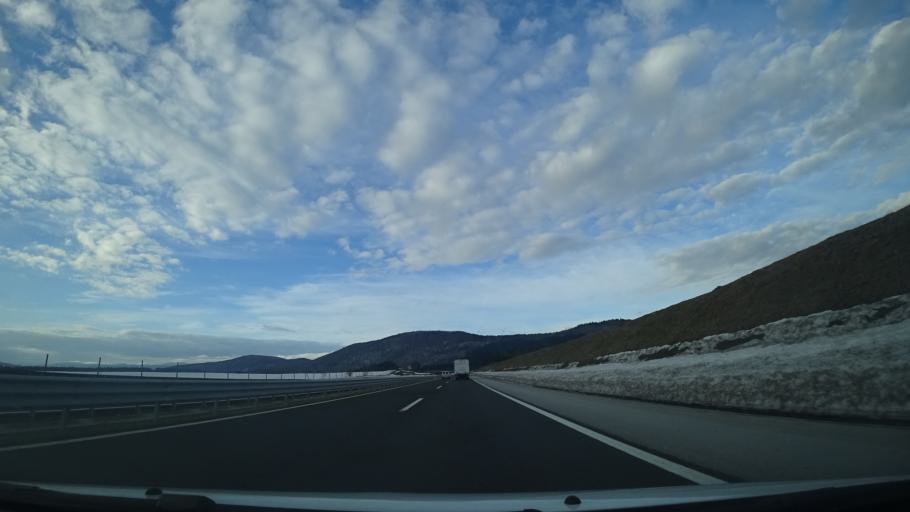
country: HR
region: Karlovacka
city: Ostarije
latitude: 45.2258
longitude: 15.2636
